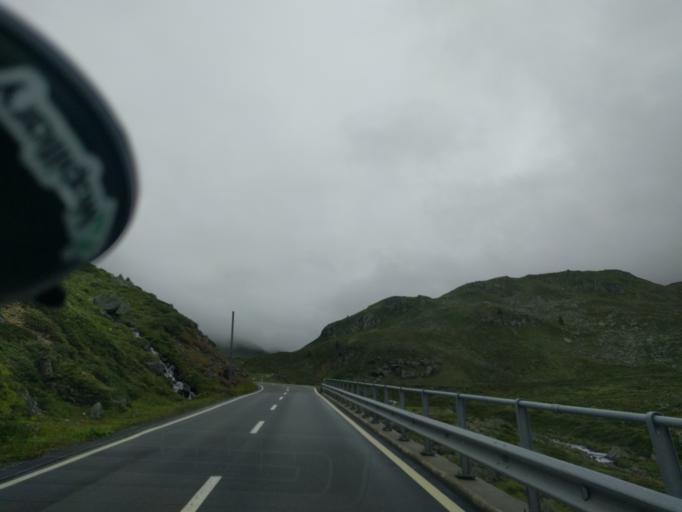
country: CH
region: Grisons
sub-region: Praettigau/Davos District
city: Davos
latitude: 46.7743
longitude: 9.9347
